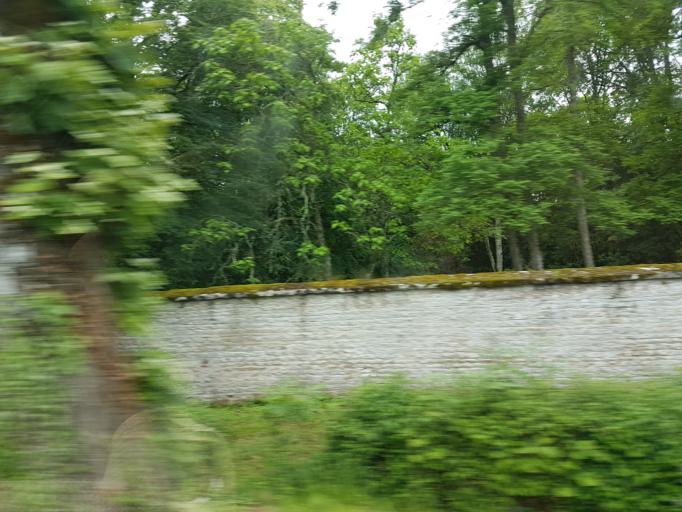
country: FR
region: Bourgogne
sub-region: Departement de la Nievre
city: Corbigny
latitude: 47.2628
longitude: 3.6779
